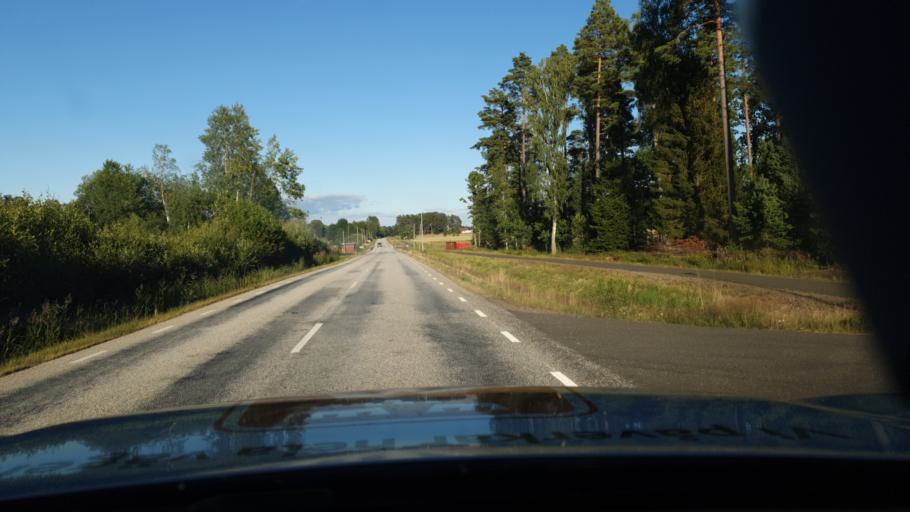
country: SE
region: Vaestra Goetaland
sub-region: Skovde Kommun
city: Stopen
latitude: 58.4793
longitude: 13.8727
